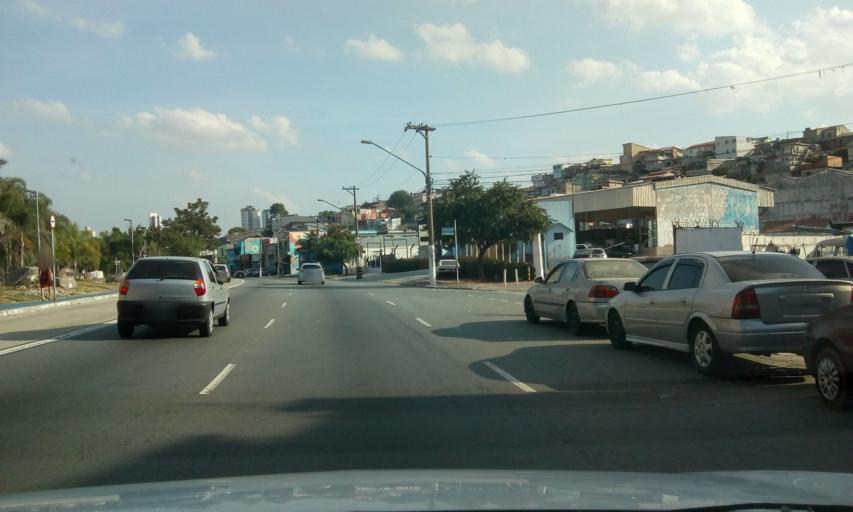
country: BR
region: Sao Paulo
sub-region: Sao Paulo
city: Sao Paulo
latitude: -23.4891
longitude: -46.6846
